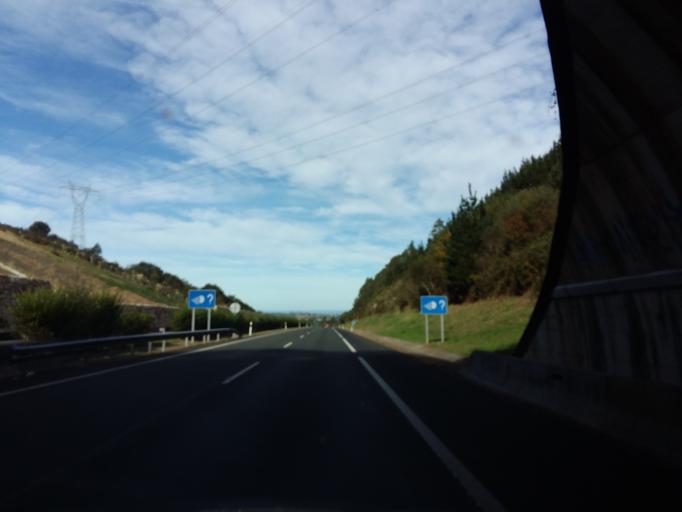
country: ES
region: Cantabria
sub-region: Provincia de Cantabria
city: Comillas
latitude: 43.3282
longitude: -4.3034
